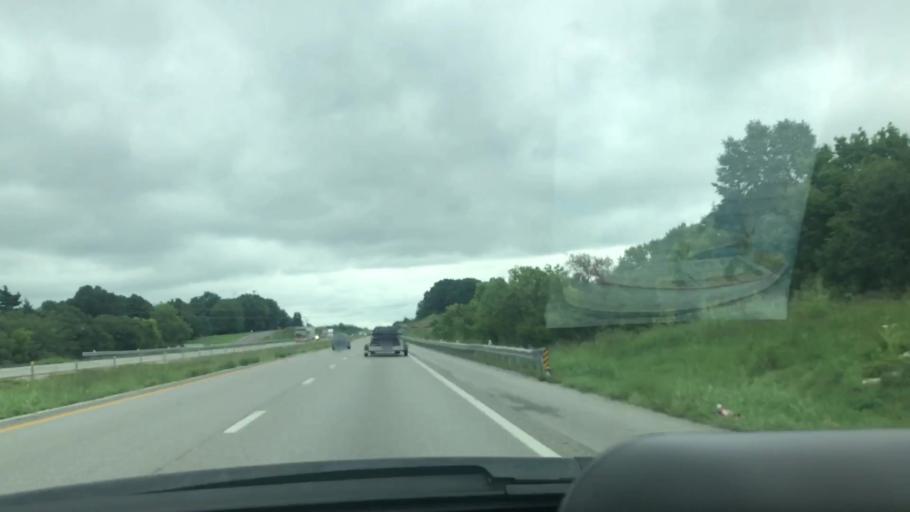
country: US
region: Missouri
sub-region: Greene County
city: Springfield
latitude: 37.2501
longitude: -93.3242
